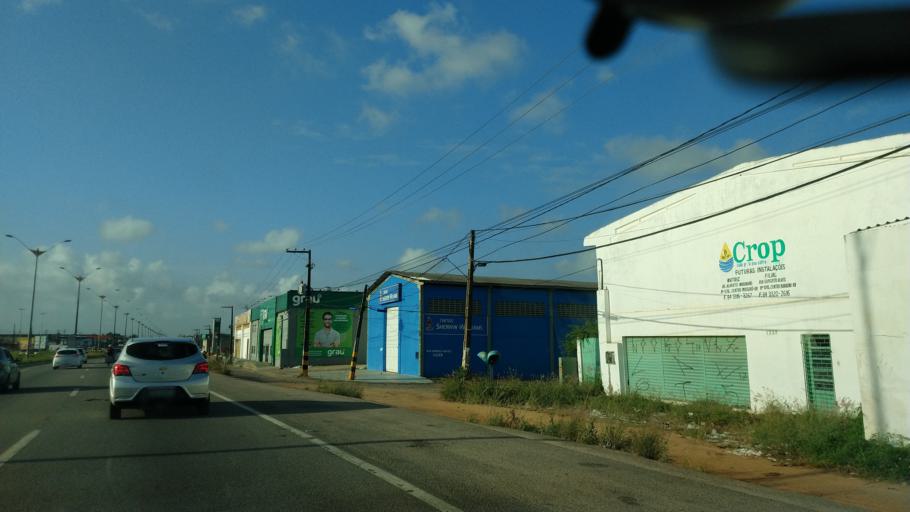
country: BR
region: Rio Grande do Norte
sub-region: Parnamirim
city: Parnamirim
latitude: -5.9044
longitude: -35.2599
